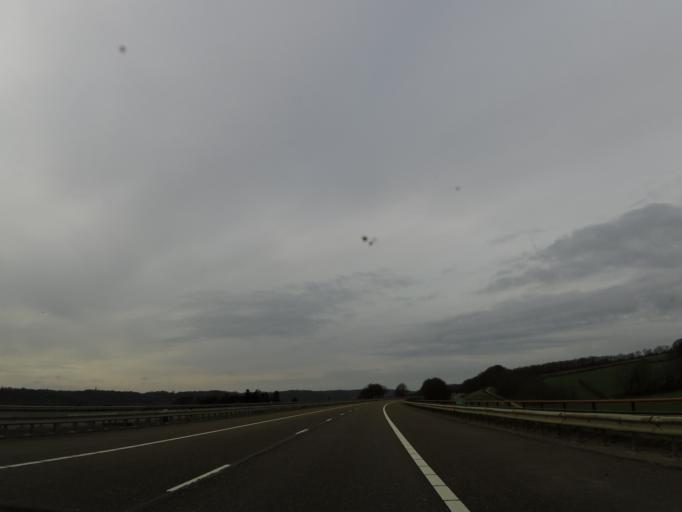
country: NL
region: Limburg
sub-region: Valkenburg aan de Geul
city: Broekhem
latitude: 50.8745
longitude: 5.8151
